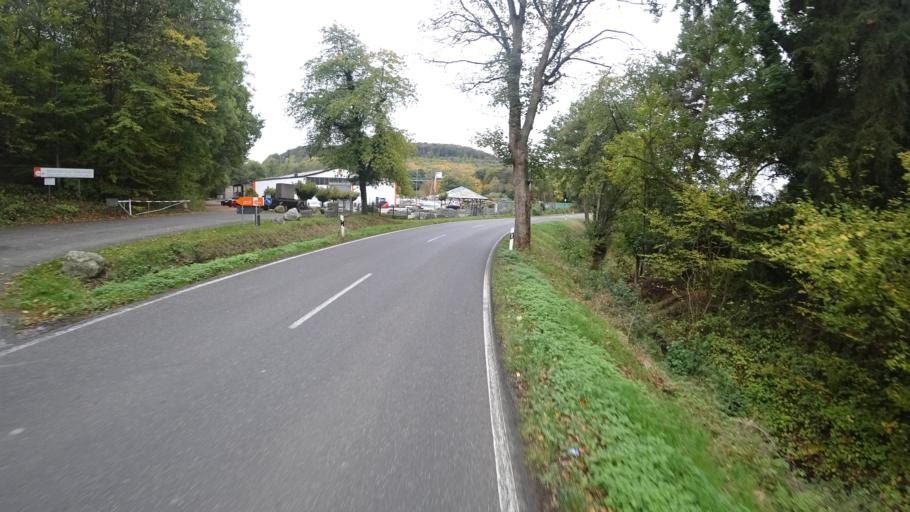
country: DE
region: Rheinland-Pfalz
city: Nordhofen
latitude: 50.5239
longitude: 7.7457
